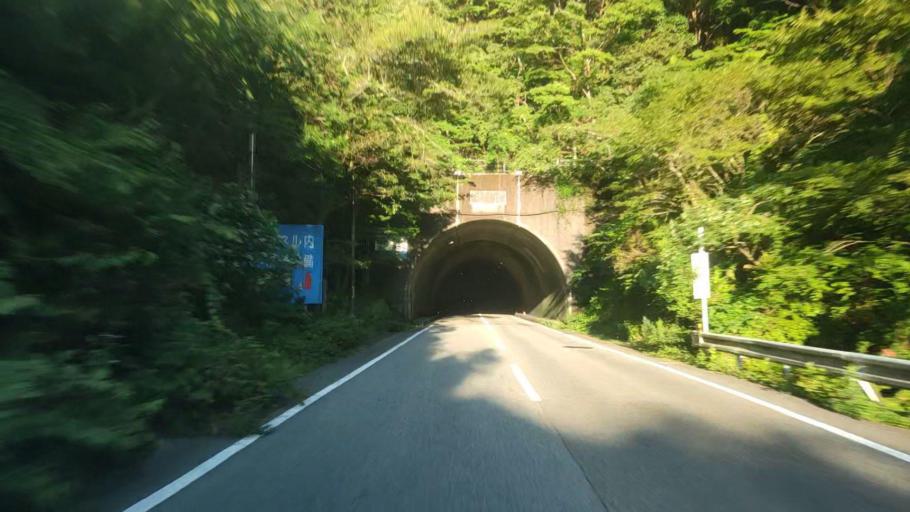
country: JP
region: Wakayama
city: Tanabe
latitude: 33.8145
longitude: 135.5782
